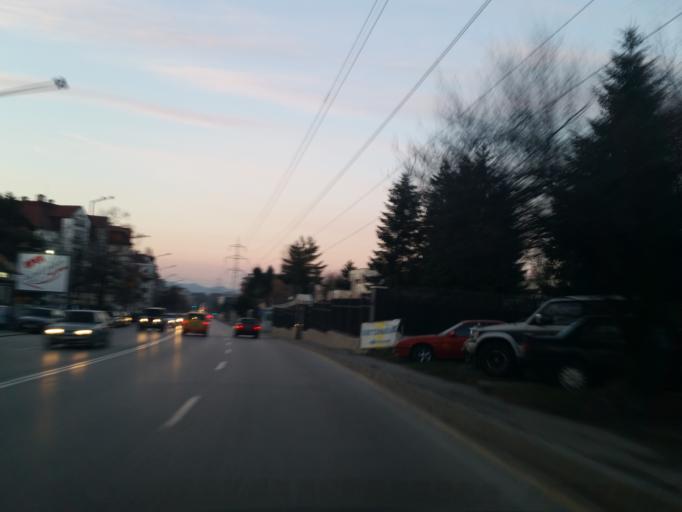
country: BG
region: Sofia-Capital
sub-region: Stolichna Obshtina
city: Sofia
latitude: 42.6474
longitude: 23.3354
